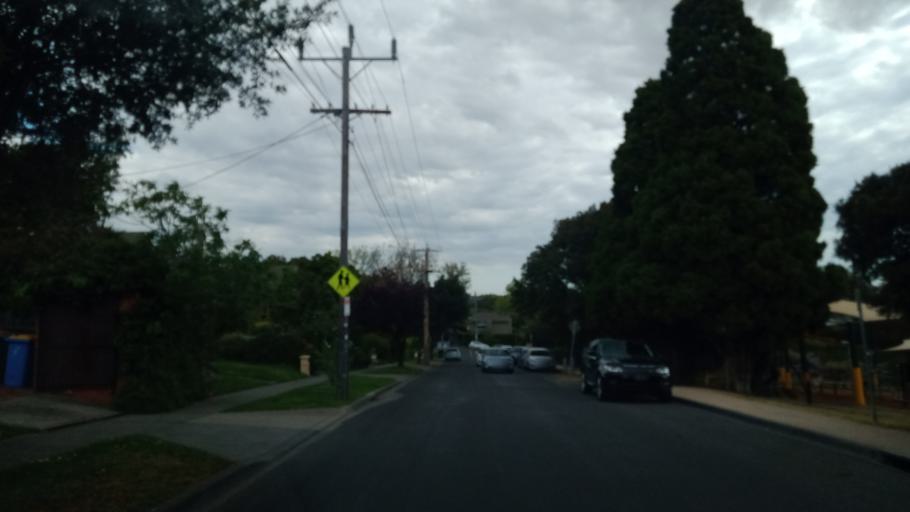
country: AU
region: Victoria
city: Glenferrie
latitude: -37.8400
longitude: 145.0505
